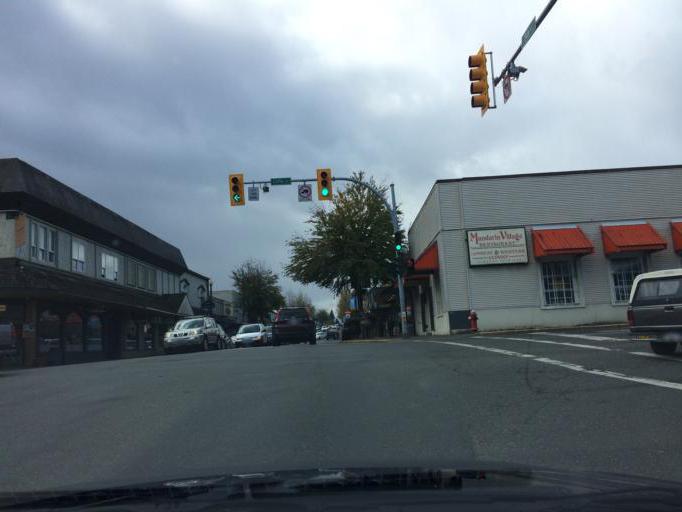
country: CA
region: British Columbia
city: Courtenay
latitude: 49.6916
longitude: -124.9970
